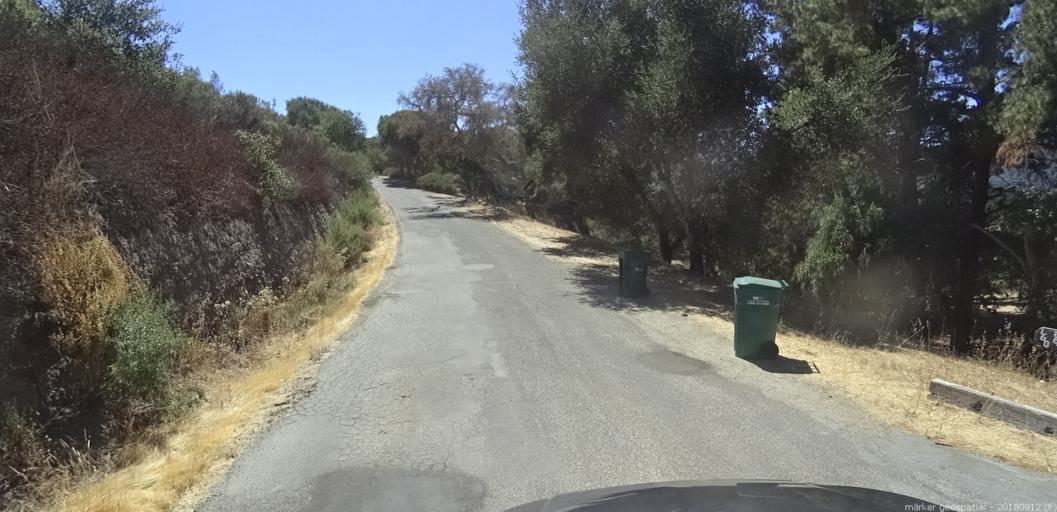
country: US
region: California
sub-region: Monterey County
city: Carmel Valley Village
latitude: 36.4868
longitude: -121.7216
